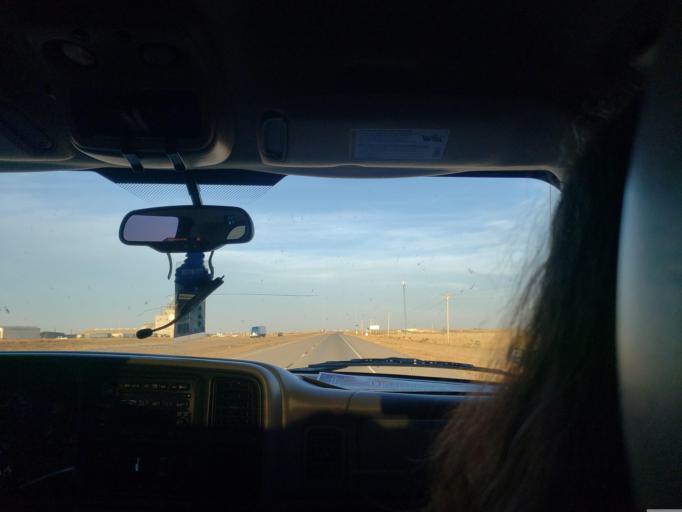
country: US
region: Oklahoma
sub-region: Texas County
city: Guymon
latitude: 36.7665
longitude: -101.3467
